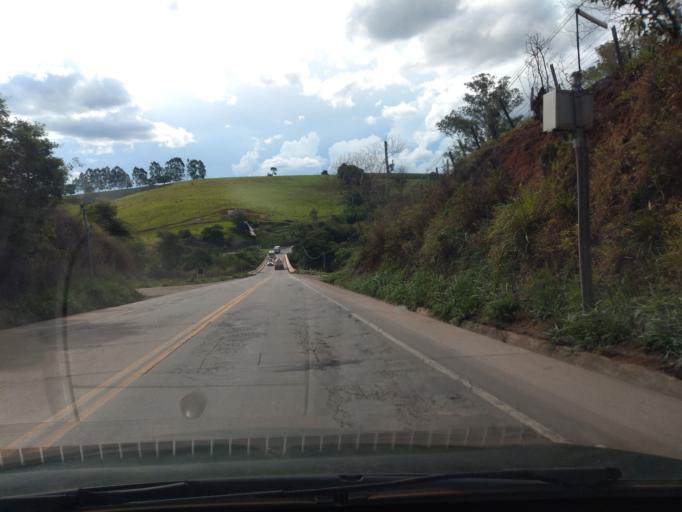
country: BR
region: Minas Gerais
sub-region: Varginha
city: Varginha
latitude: -21.6124
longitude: -45.4288
